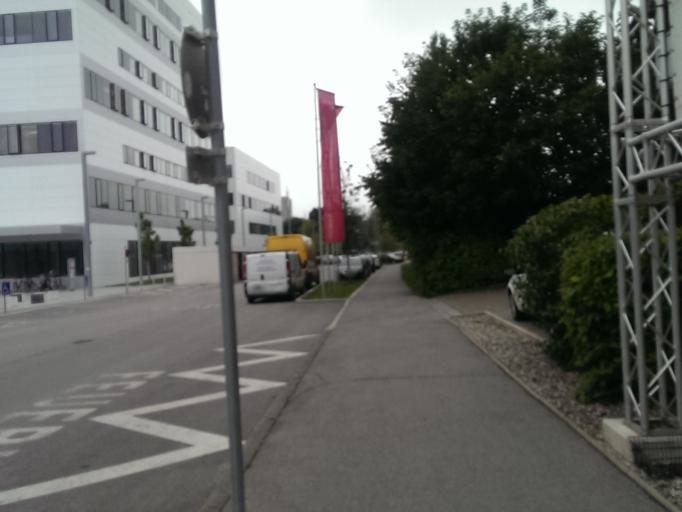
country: AT
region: Styria
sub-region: Graz Stadt
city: Graz
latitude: 47.0598
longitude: 15.4636
